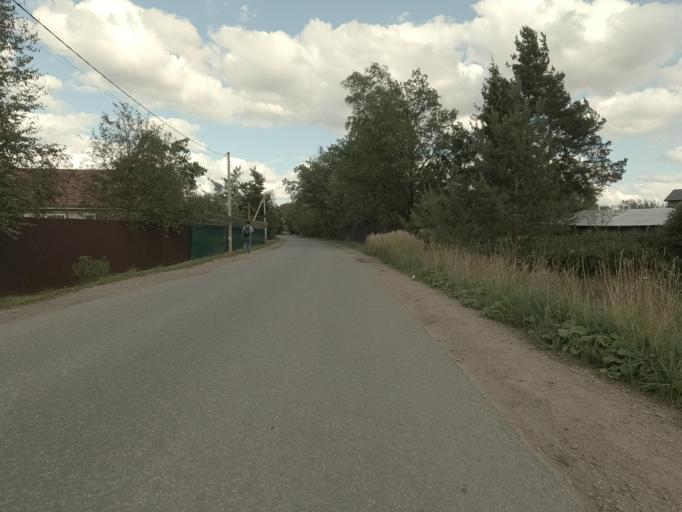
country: RU
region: Leningrad
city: Ul'yanovka
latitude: 59.6337
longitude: 30.7707
